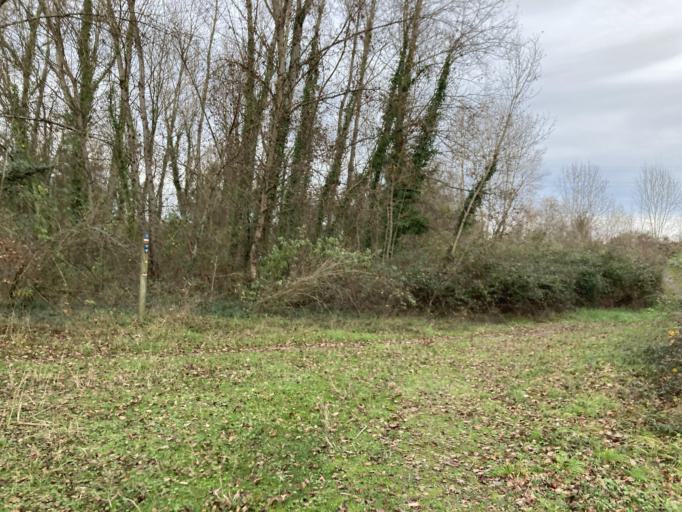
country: FR
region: Aquitaine
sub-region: Departement des Pyrenees-Atlantiques
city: Artiguelouve
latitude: 43.3322
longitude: -0.4655
